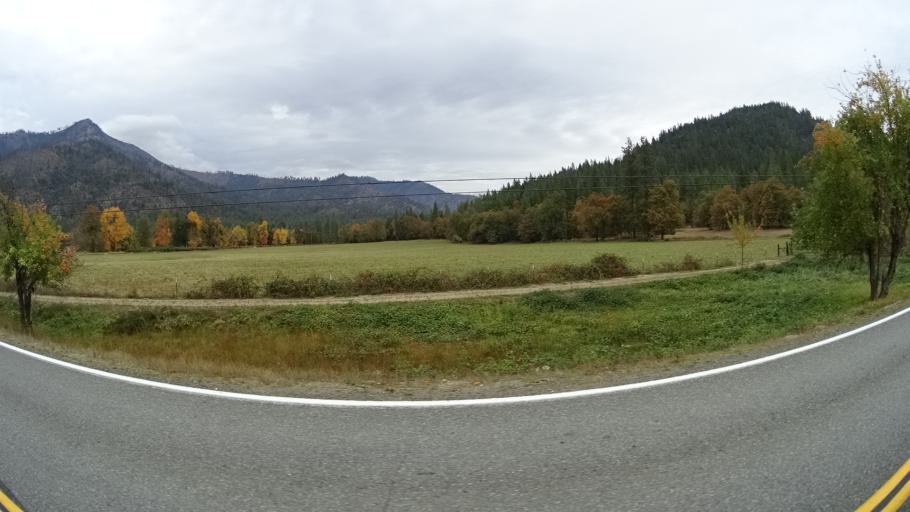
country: US
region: California
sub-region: Siskiyou County
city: Happy Camp
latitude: 41.8396
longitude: -123.1906
